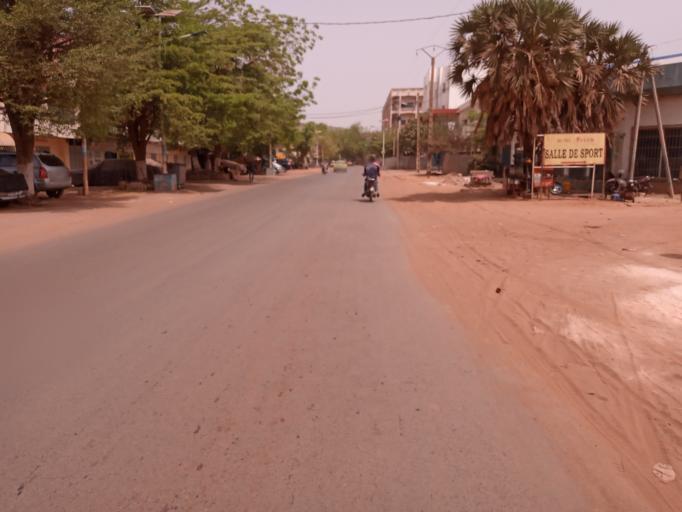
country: ML
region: Bamako
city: Bamako
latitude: 12.6488
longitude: -7.9806
